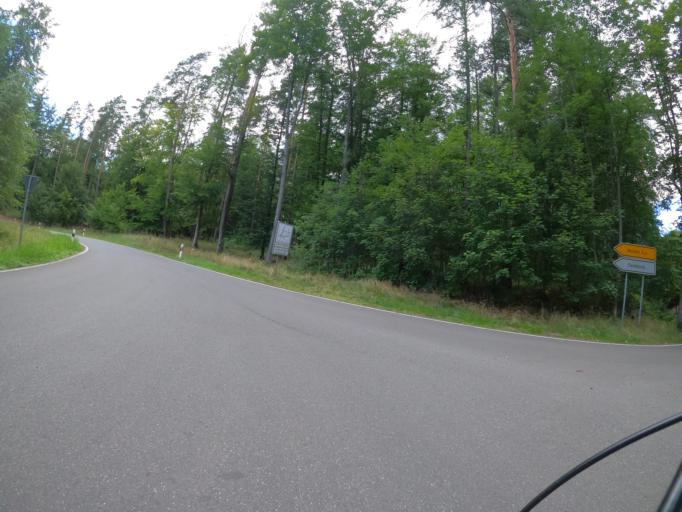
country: DE
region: Brandenburg
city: Angermunde
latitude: 53.0494
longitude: 13.9009
